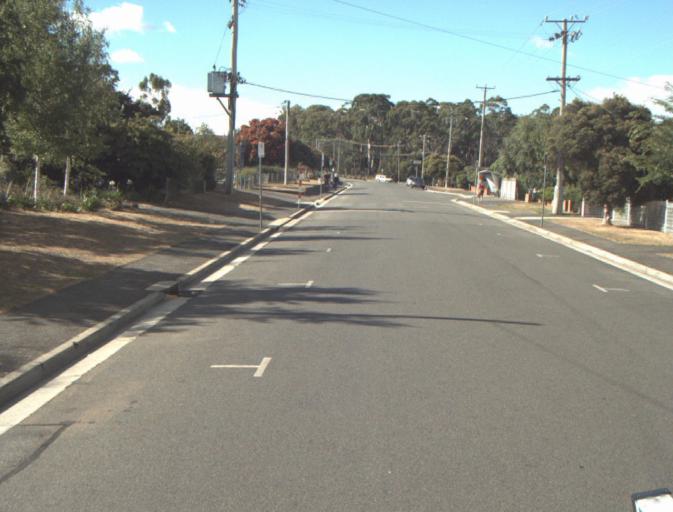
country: AU
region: Tasmania
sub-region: Launceston
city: Newstead
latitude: -41.4621
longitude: 147.1729
